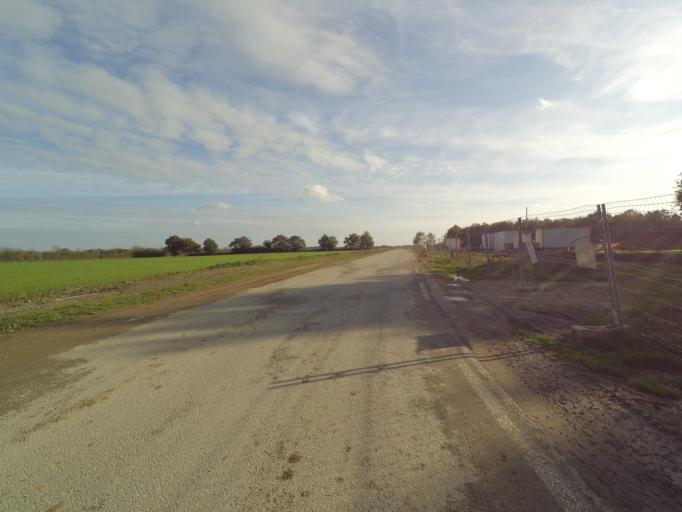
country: FR
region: Pays de la Loire
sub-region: Departement de la Vendee
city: Saint-Hilaire-de-Loulay
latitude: 47.0207
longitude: -1.3481
